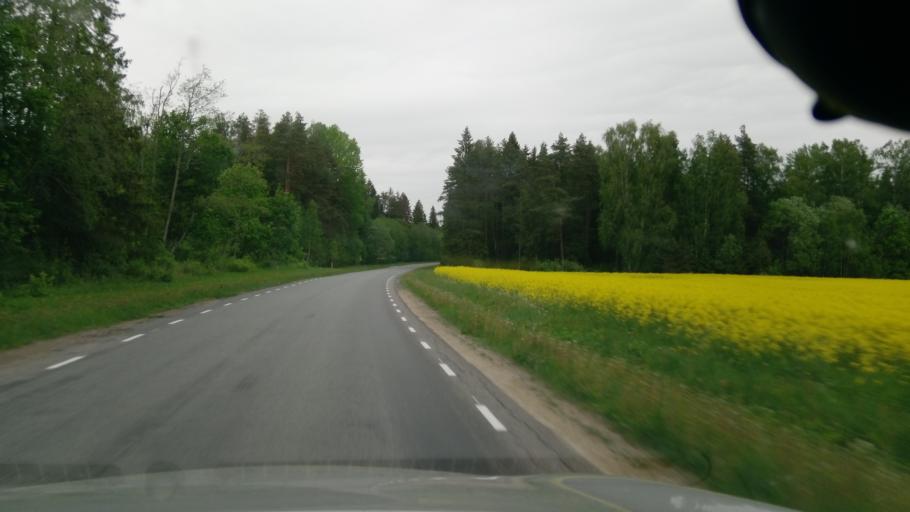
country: EE
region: Jaervamaa
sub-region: Koeru vald
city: Koeru
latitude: 58.9854
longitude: 26.0498
